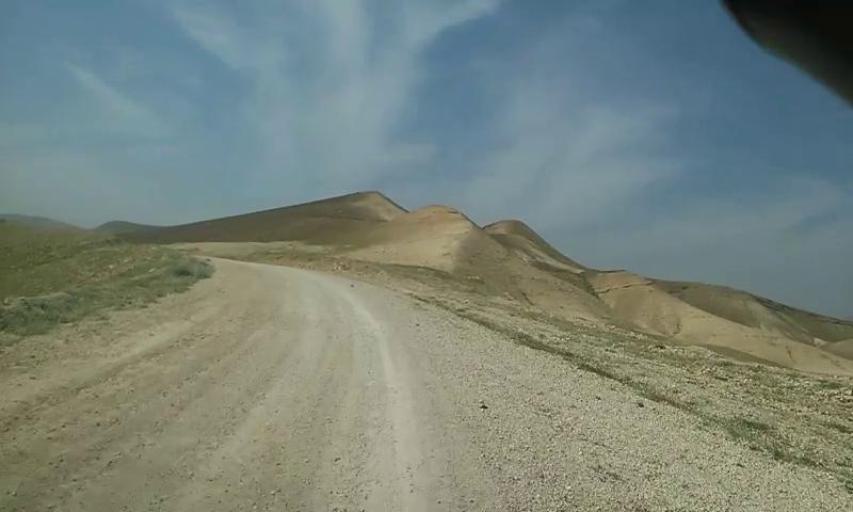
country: PS
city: `Arab ar Rashaydah
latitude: 31.4851
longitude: 35.2749
